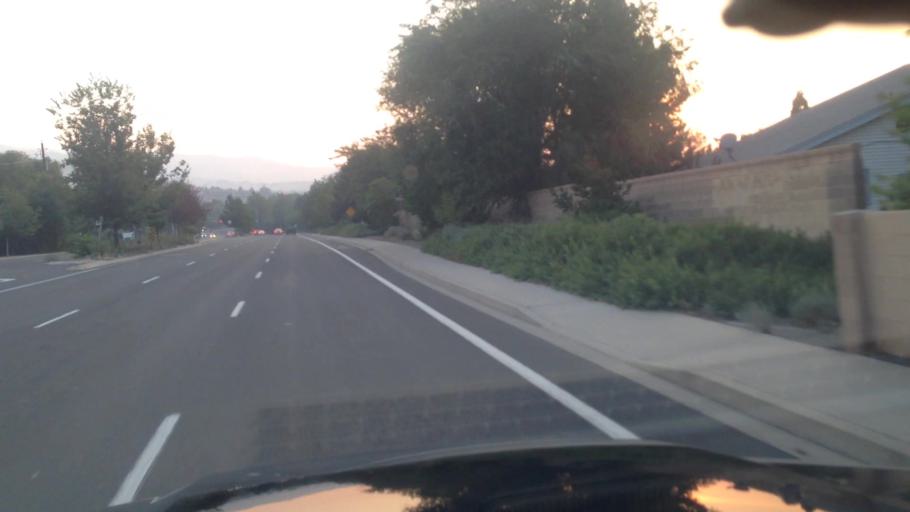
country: US
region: Nevada
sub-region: Washoe County
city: Reno
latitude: 39.4768
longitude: -119.8031
